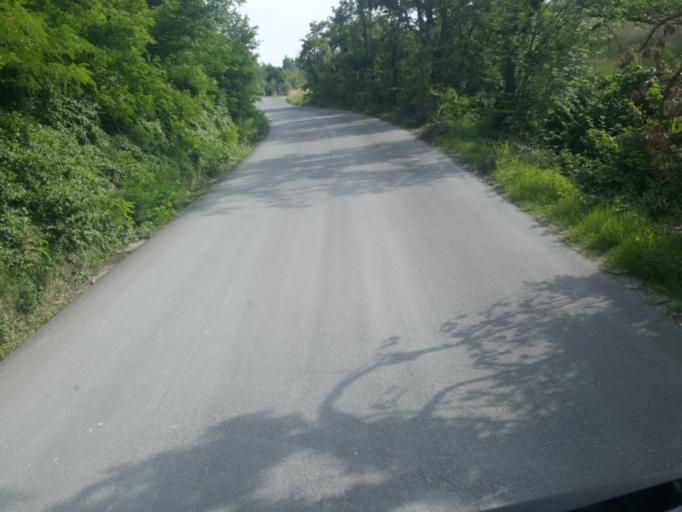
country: IT
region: Emilia-Romagna
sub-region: Provincia di Piacenza
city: Ponte dell'Olio
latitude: 44.8744
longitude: 9.6243
